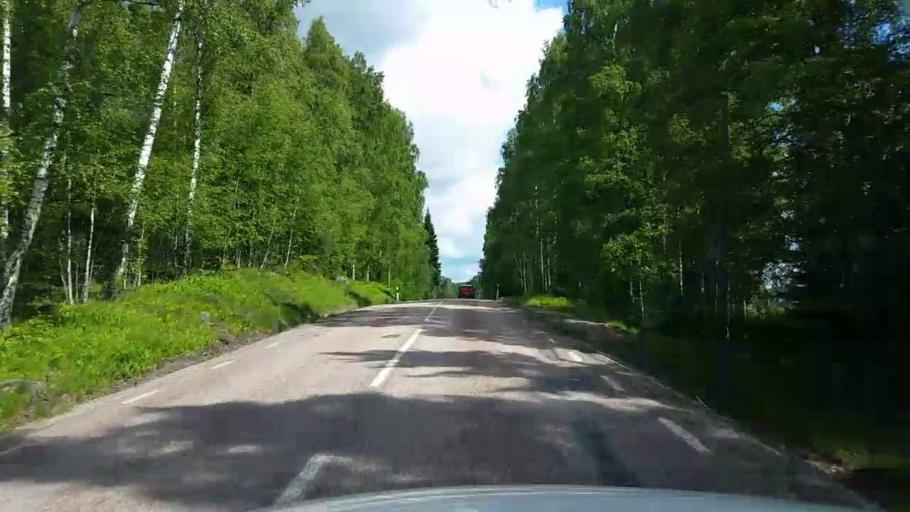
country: SE
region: Vaestmanland
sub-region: Skinnskattebergs Kommun
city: Skinnskatteberg
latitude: 59.7438
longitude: 15.8094
